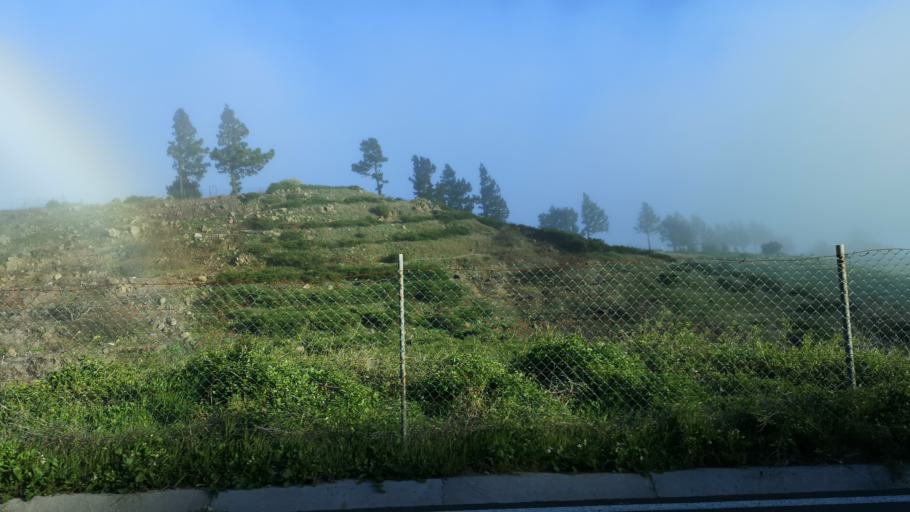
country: ES
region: Canary Islands
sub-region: Provincia de Santa Cruz de Tenerife
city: Alajero
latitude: 28.0992
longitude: -17.2481
